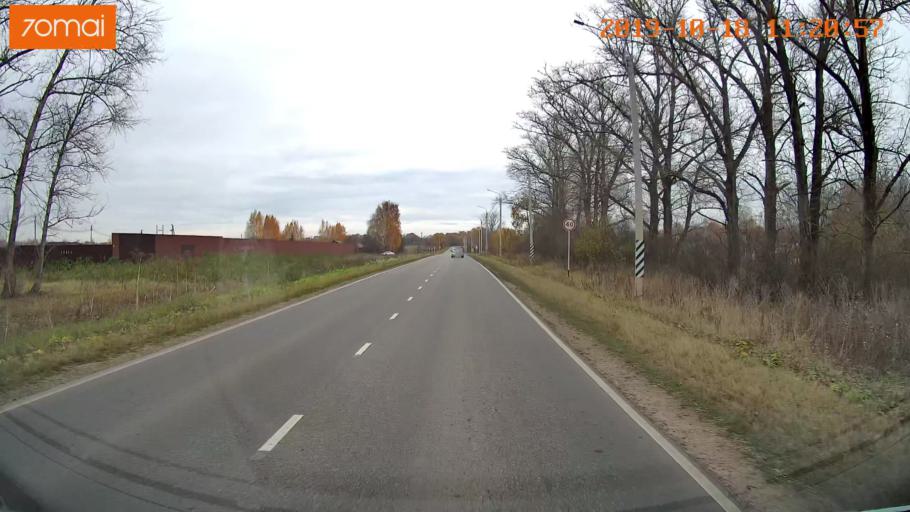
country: RU
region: Tula
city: Kimovsk
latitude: 54.0681
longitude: 38.5615
